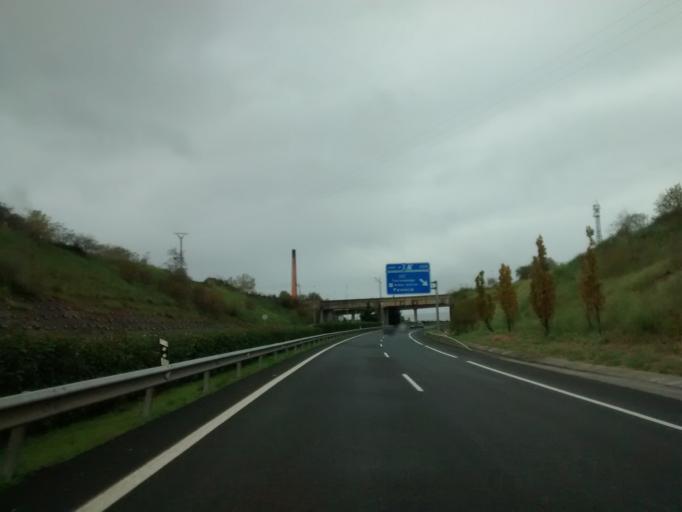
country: ES
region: Cantabria
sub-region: Provincia de Cantabria
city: Torrelavega
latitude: 43.3446
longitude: -4.0202
